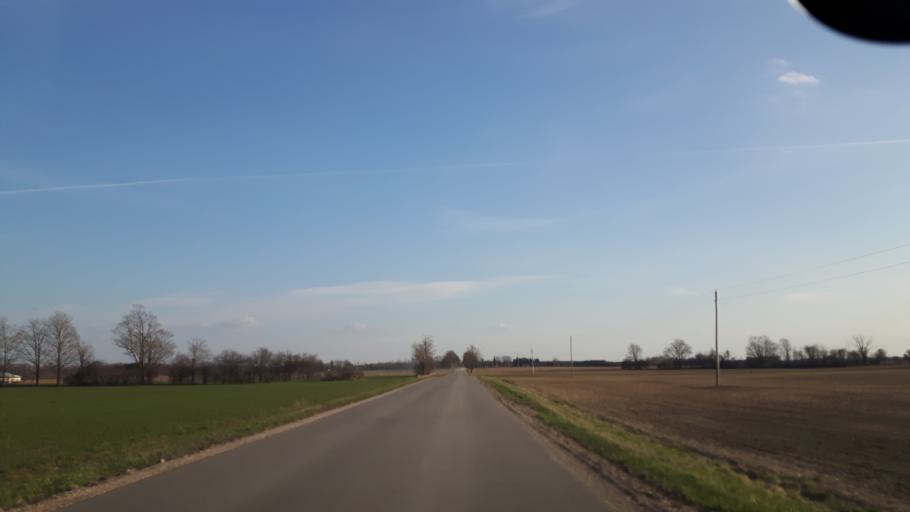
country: CA
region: Ontario
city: Goderich
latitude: 43.6352
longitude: -81.6644
